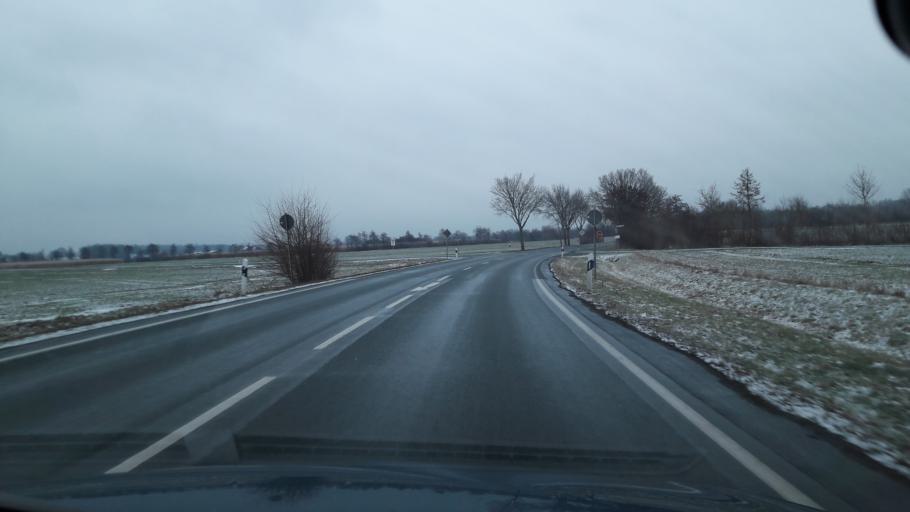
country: DE
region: North Rhine-Westphalia
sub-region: Regierungsbezirk Munster
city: Wadersloh
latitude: 51.7292
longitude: 8.2610
